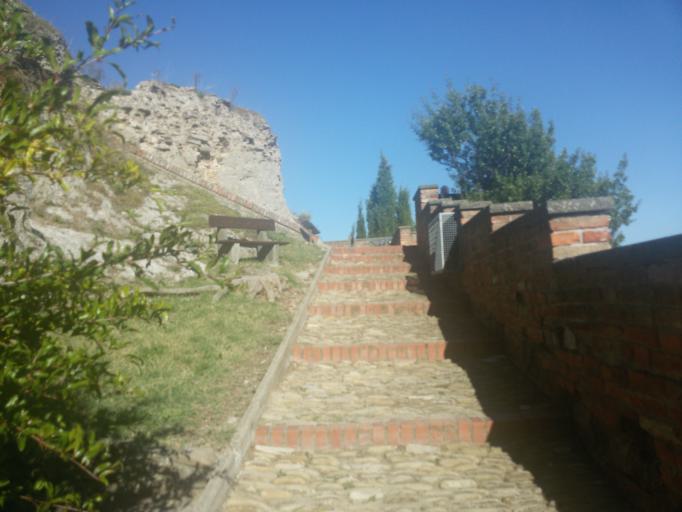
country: IT
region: Emilia-Romagna
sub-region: Provincia di Ravenna
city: Brisighella
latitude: 44.2242
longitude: 11.7737
